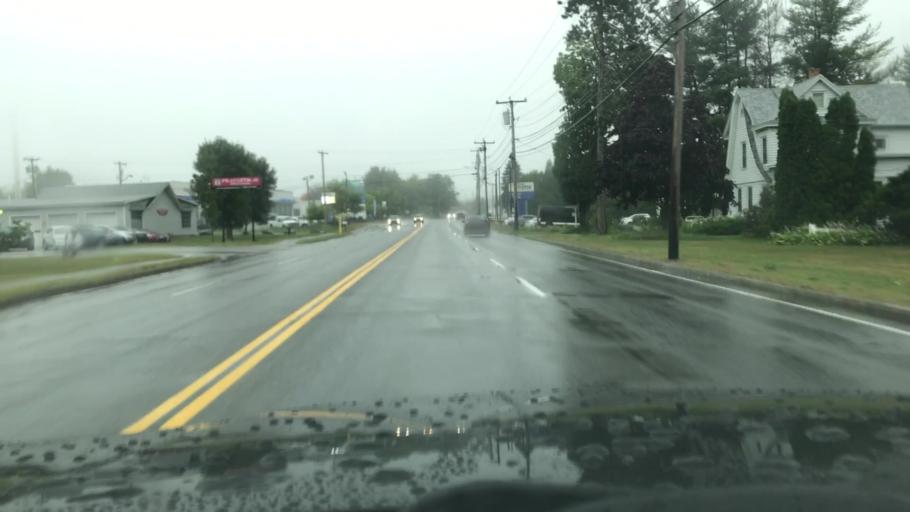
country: US
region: Maine
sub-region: York County
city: Saco
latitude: 43.5240
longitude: -70.4279
